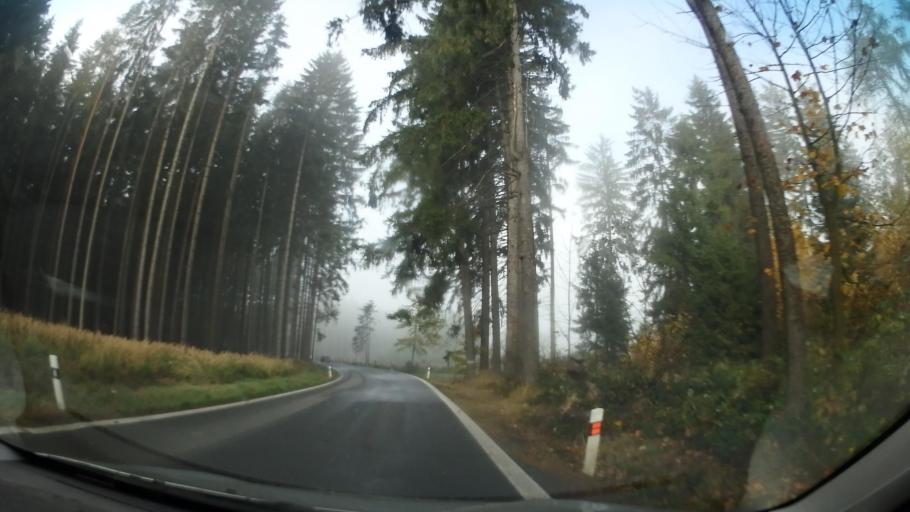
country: CZ
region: Vysocina
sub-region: Okres Zd'ar nad Sazavou
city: Nove Mesto na Morave
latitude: 49.4786
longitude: 16.0388
